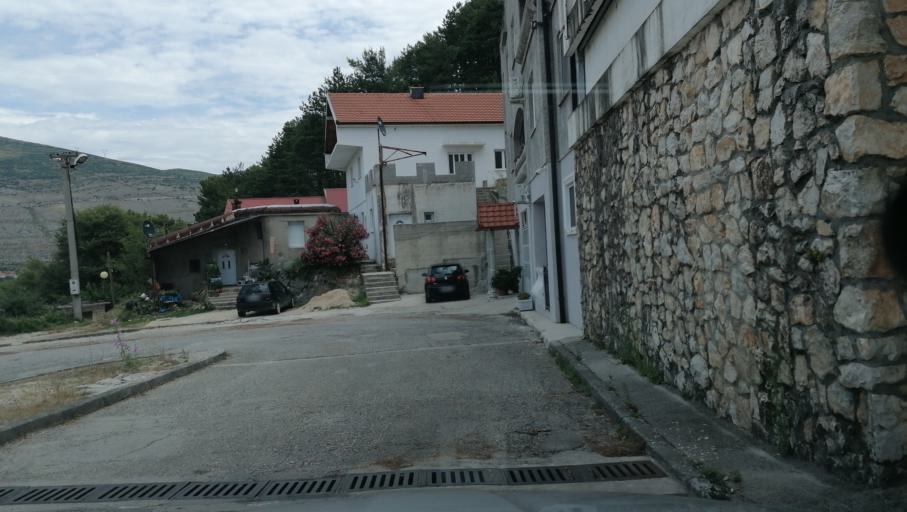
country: BA
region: Republika Srpska
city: Trebinje
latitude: 42.7121
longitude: 18.3578
